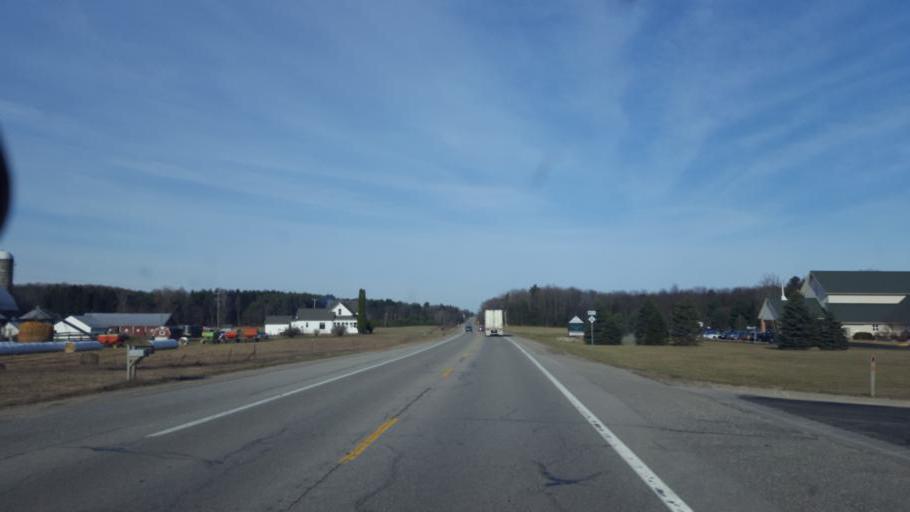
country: US
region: Michigan
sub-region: Montcalm County
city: Lakeview
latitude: 43.4309
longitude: -85.2138
